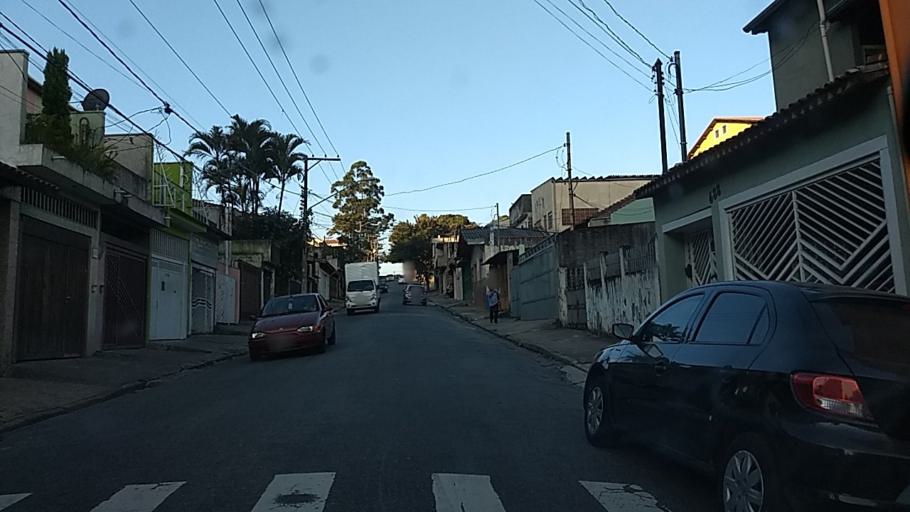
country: BR
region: Sao Paulo
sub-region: Sao Paulo
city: Sao Paulo
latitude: -23.4928
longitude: -46.6041
